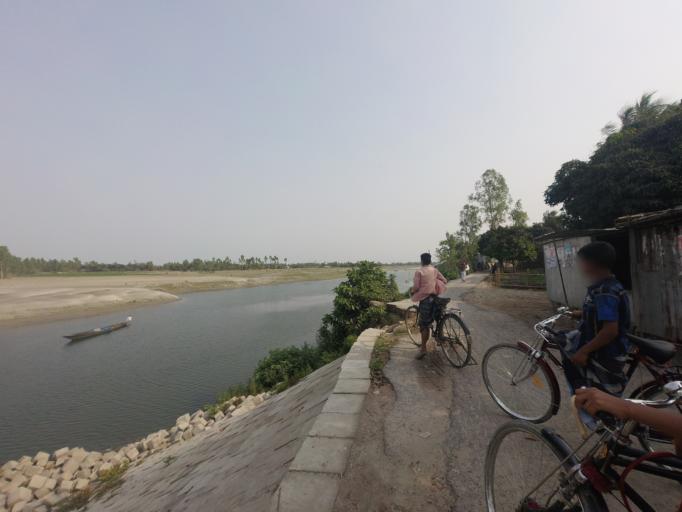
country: BD
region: Rajshahi
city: Sirajganj
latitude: 24.3313
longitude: 89.7149
